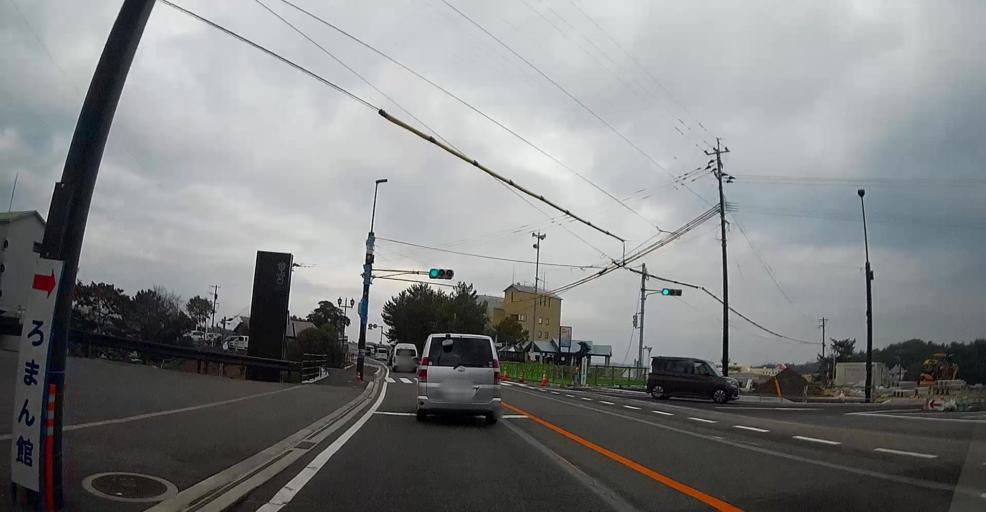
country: JP
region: Kumamoto
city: Yatsushiro
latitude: 32.5260
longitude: 130.4250
